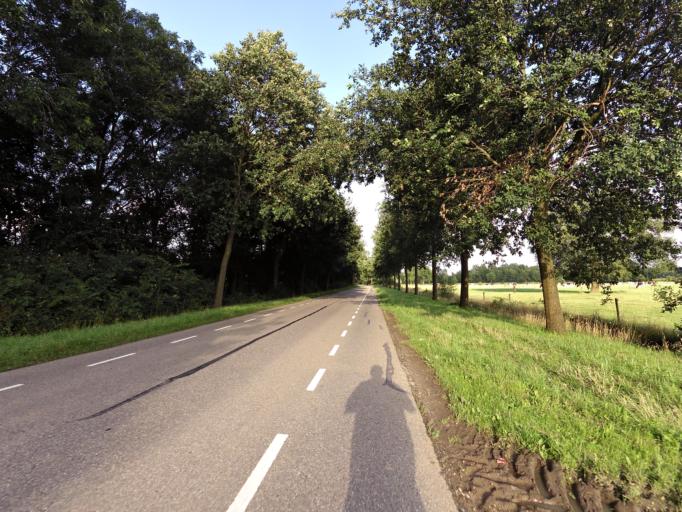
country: NL
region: Gelderland
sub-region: Gemeente Doesburg
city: Doesburg
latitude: 51.9911
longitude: 6.1511
